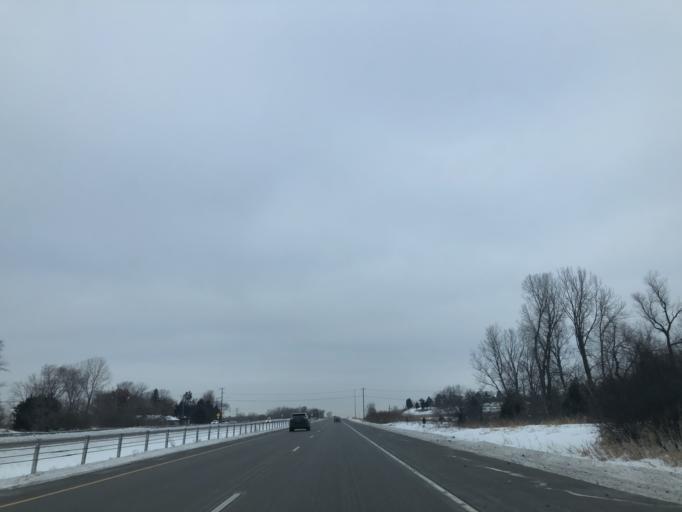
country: US
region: Minnesota
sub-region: Ramsey County
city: Shoreview
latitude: 45.0766
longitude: -93.1728
